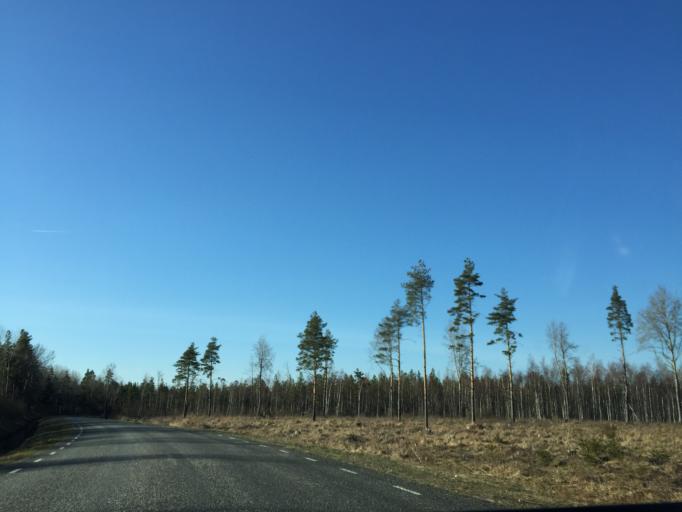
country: RU
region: Pskov
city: Gdov
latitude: 59.0086
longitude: 27.6860
